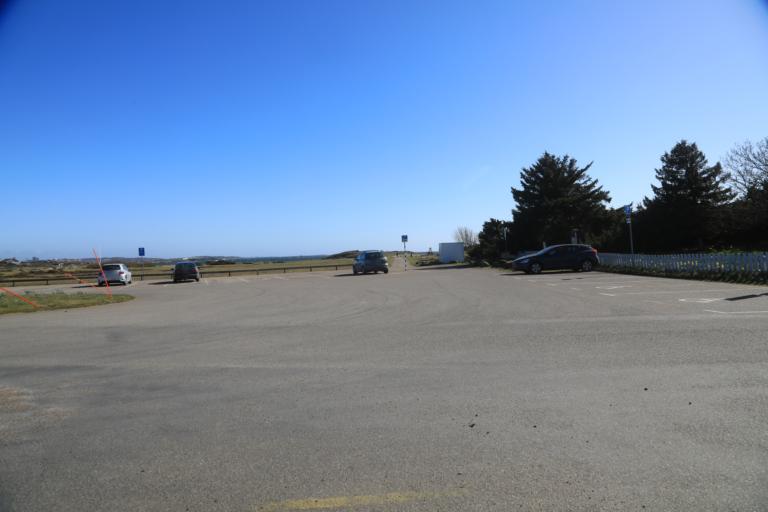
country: SE
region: Halland
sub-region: Varbergs Kommun
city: Varberg
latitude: 57.1197
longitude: 12.2002
